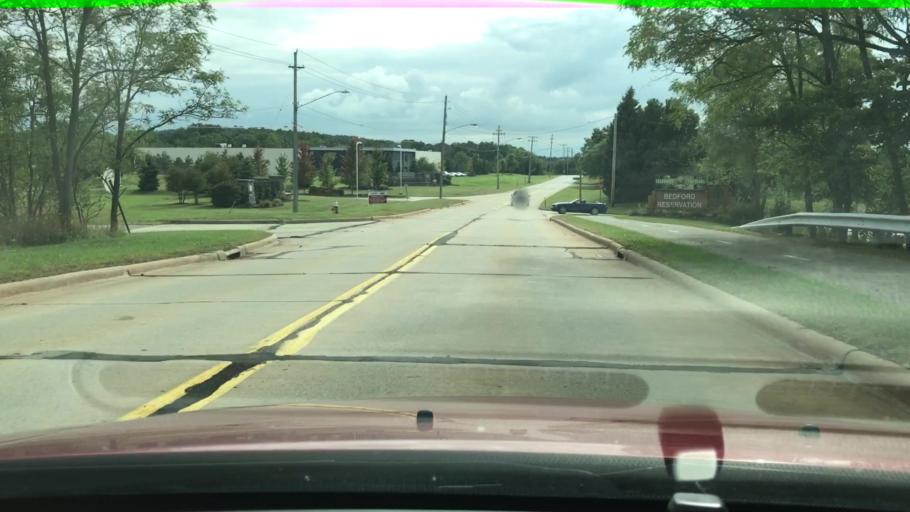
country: US
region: Ohio
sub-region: Cuyahoga County
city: Bedford
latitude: 41.3805
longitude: -81.5338
